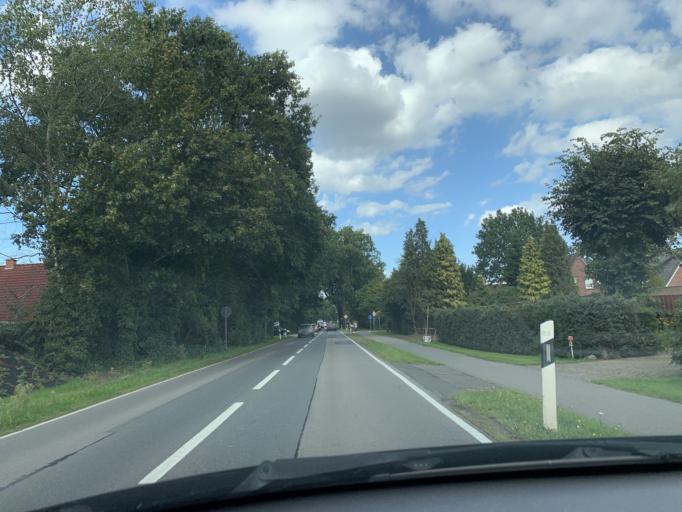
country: DE
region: Lower Saxony
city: Bad Zwischenahn
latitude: 53.1621
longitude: 7.9973
